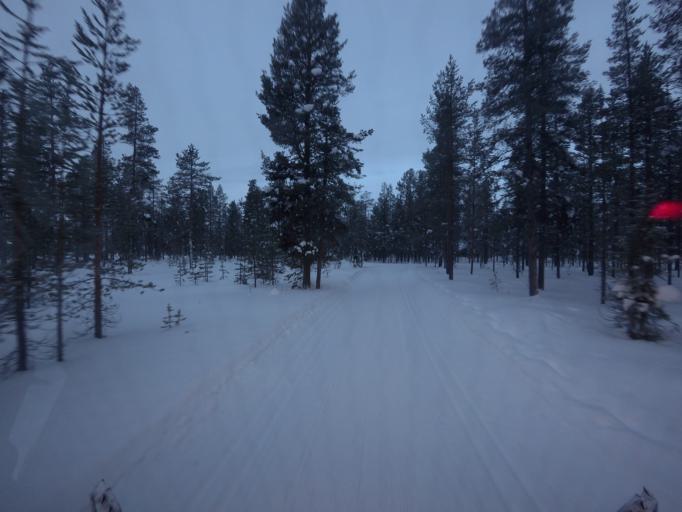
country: FI
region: Lapland
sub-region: Tunturi-Lappi
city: Kolari
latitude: 67.6241
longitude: 24.1717
